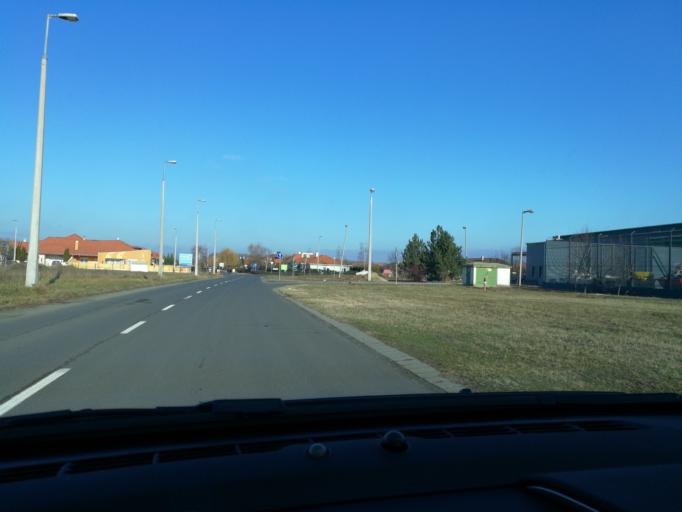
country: HU
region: Szabolcs-Szatmar-Bereg
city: Nyiregyhaza
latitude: 47.9721
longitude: 21.7339
